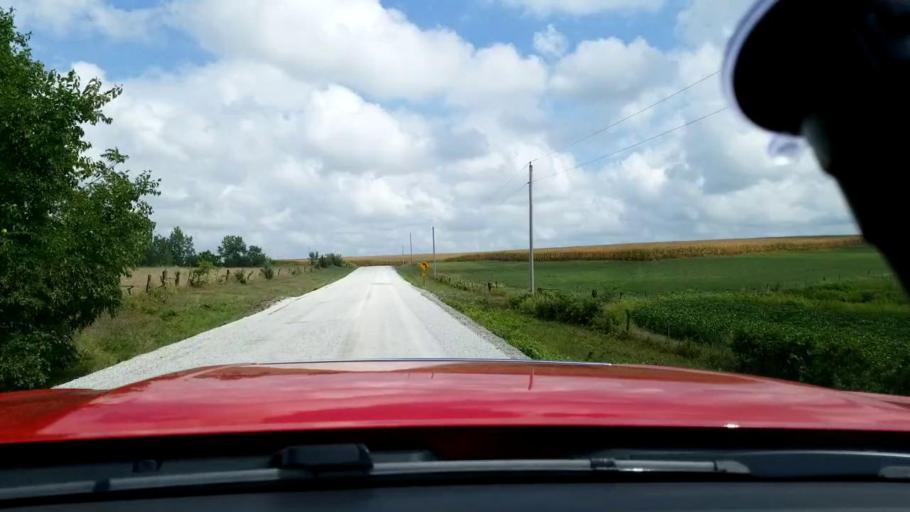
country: US
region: Iowa
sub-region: Decatur County
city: Lamoni
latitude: 40.6563
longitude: -94.0501
